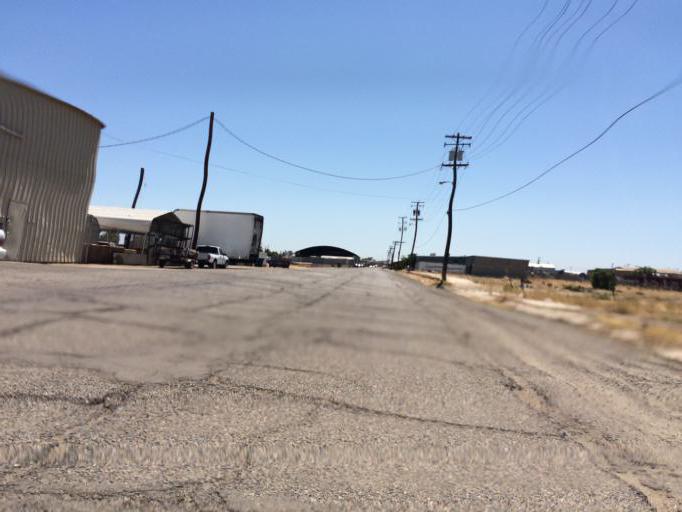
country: US
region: California
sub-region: Fresno County
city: Fresno
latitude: 36.7325
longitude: -119.7767
